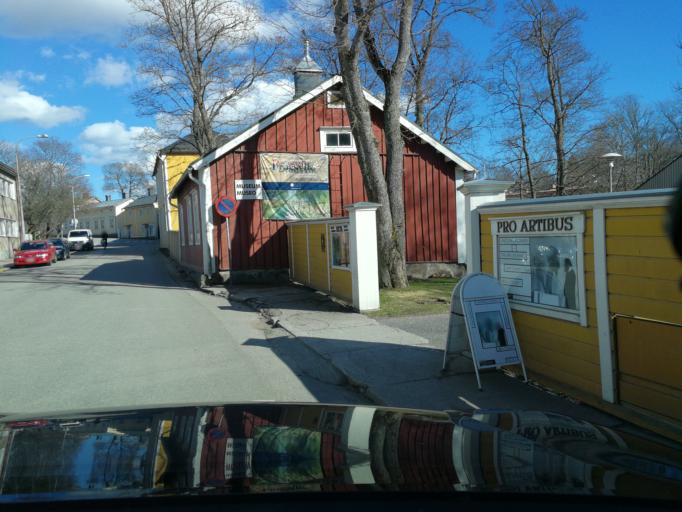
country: FI
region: Uusimaa
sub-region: Raaseporin
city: Ekenaes
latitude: 59.9742
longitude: 23.4375
